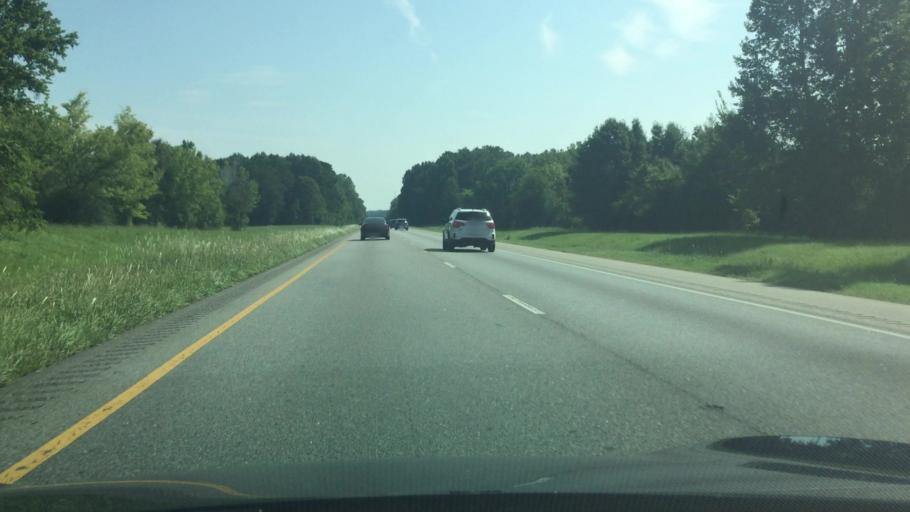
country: US
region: Alabama
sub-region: Lowndes County
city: Hayneville
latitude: 32.2159
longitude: -86.4013
